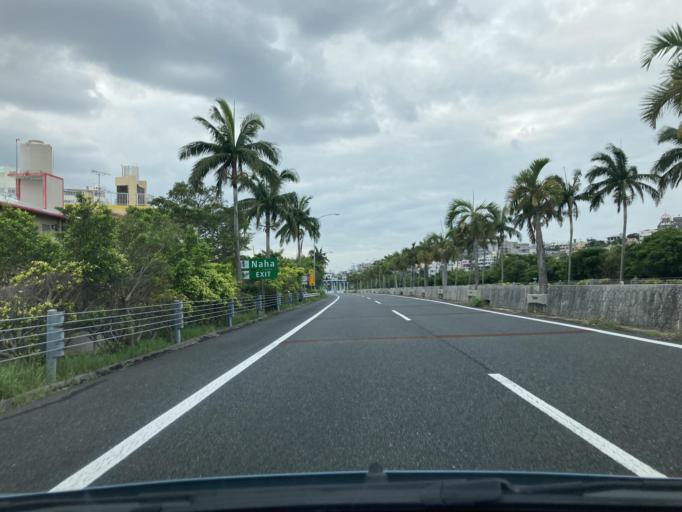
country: JP
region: Okinawa
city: Naha-shi
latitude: 26.2124
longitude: 127.7292
